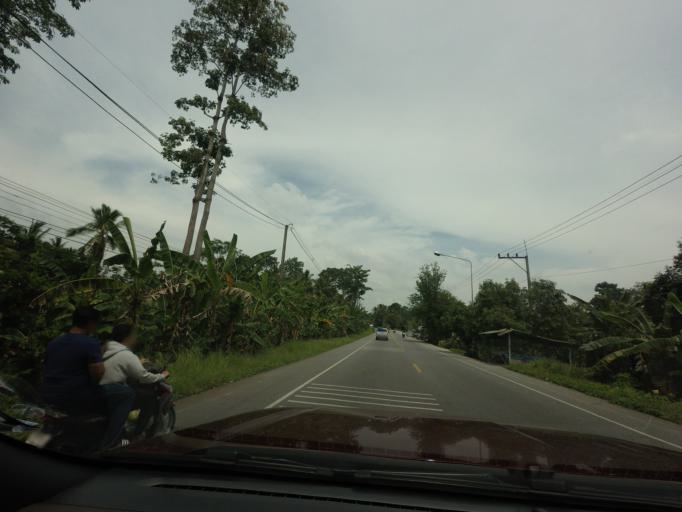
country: TH
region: Yala
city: Yala
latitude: 6.6048
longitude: 101.3035
